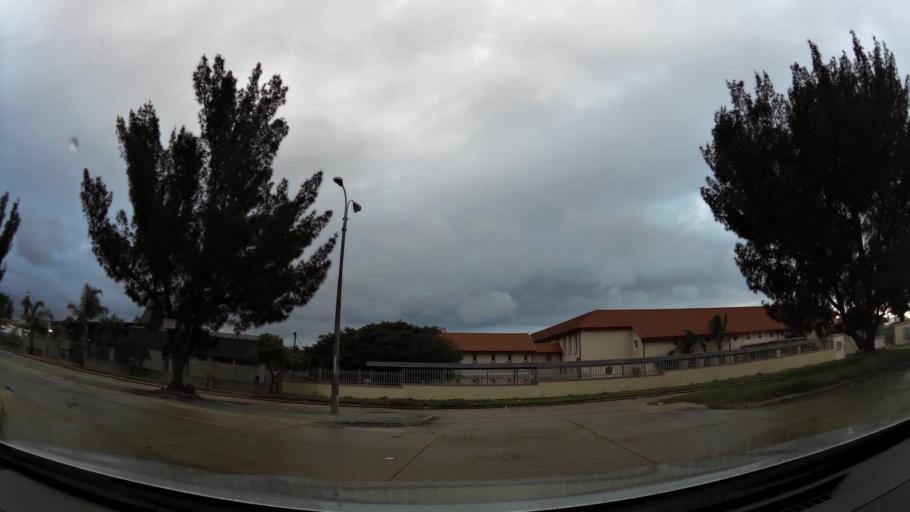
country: ZA
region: Eastern Cape
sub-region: Nelson Mandela Bay Metropolitan Municipality
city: Port Elizabeth
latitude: -33.9208
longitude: 25.5941
